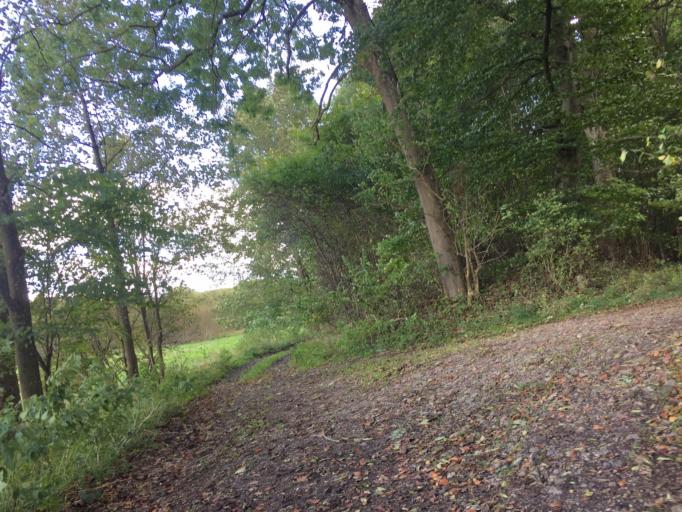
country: DK
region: Zealand
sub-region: Koge Kommune
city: Borup
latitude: 55.4723
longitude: 11.8966
